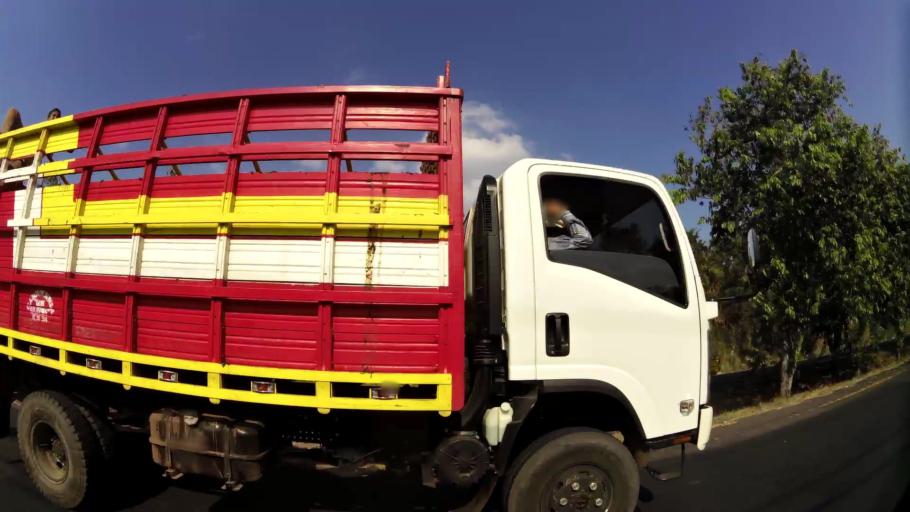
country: SV
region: San Salvador
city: Soyapango
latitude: 13.7135
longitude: -89.1266
